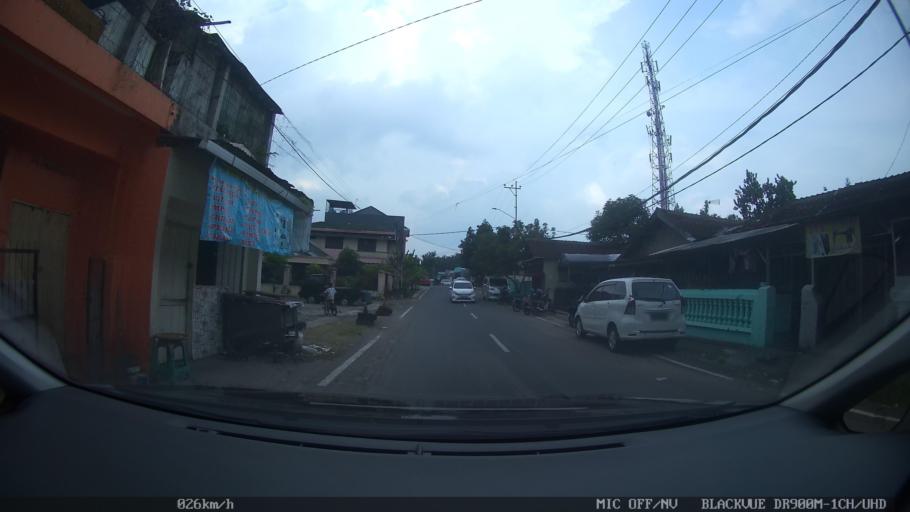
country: ID
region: Lampung
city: Bandarlampung
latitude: -5.4261
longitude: 105.2526
